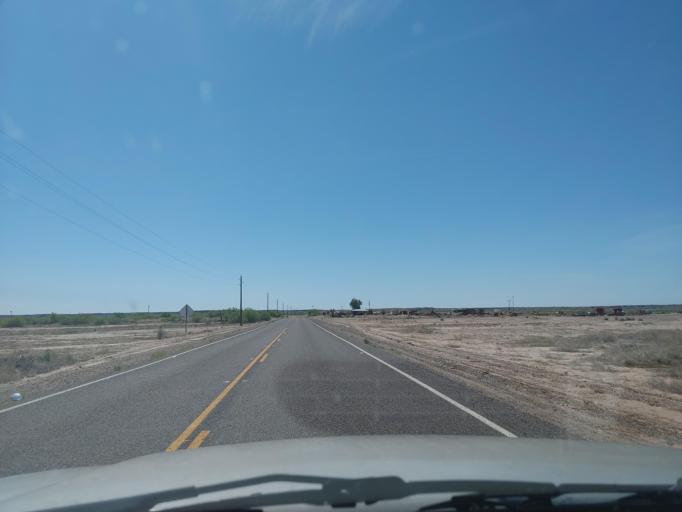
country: US
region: Arizona
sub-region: Maricopa County
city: Gila Bend
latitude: 32.9601
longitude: -113.3059
